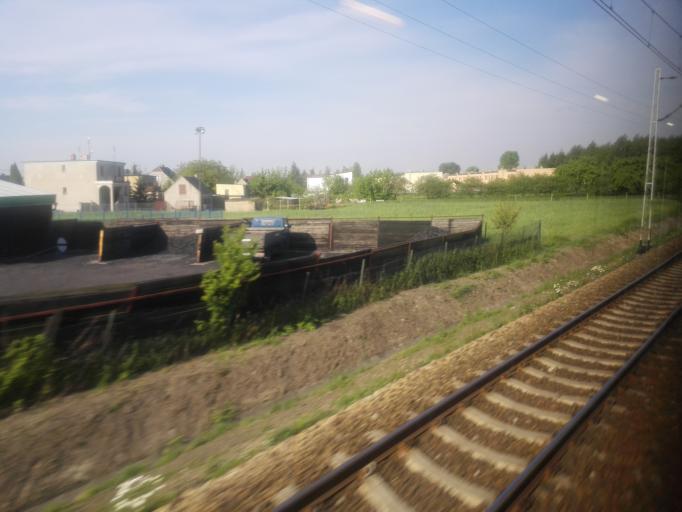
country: PL
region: Greater Poland Voivodeship
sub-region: Powiat wrzesinski
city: Wrzesnia
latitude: 52.3364
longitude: 17.5978
